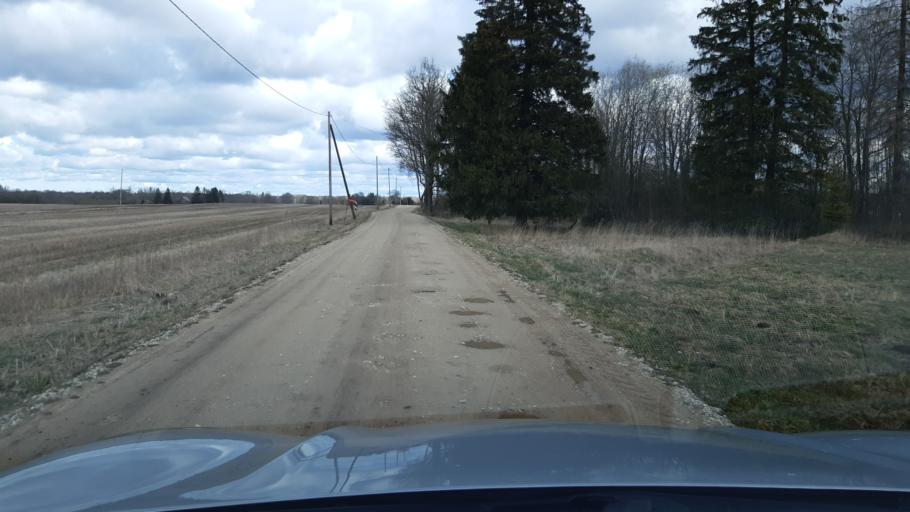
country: EE
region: Harju
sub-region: Rae vald
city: Vaida
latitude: 59.0796
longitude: 25.1215
